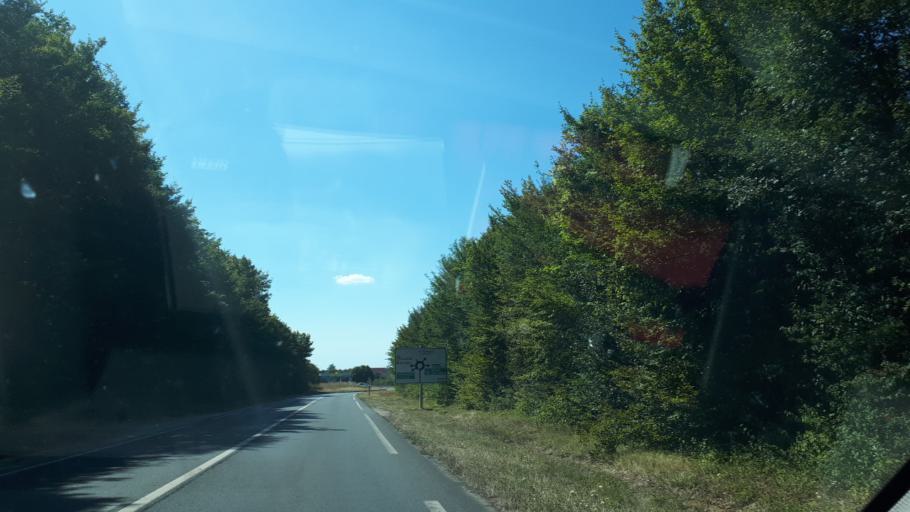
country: FR
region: Centre
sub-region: Departement du Loir-et-Cher
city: Vineuil
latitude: 47.5615
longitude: 1.3769
